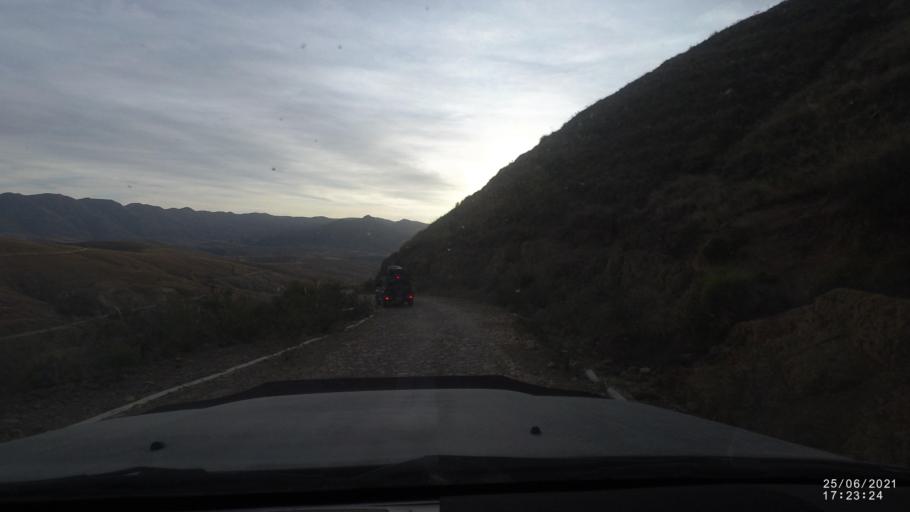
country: BO
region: Cochabamba
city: Mizque
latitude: -17.9119
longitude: -65.6876
